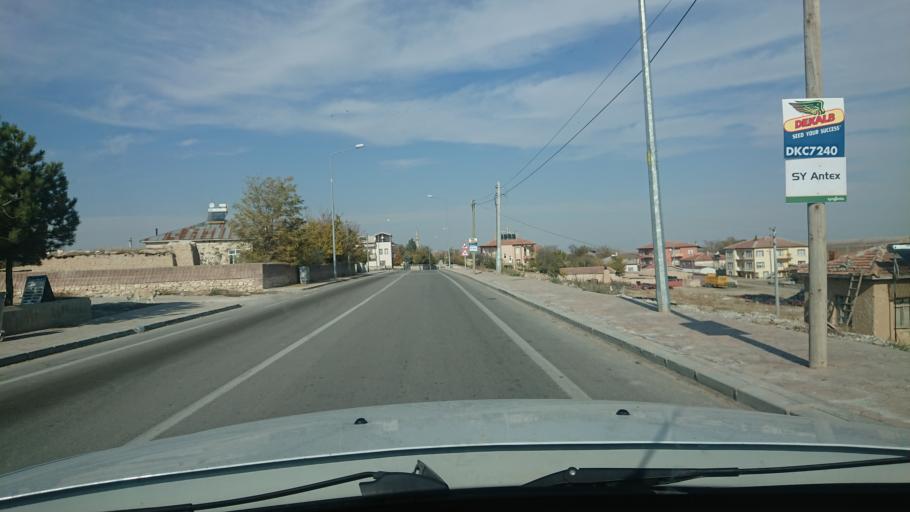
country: TR
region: Aksaray
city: Sultanhani
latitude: 38.2486
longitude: 33.4490
